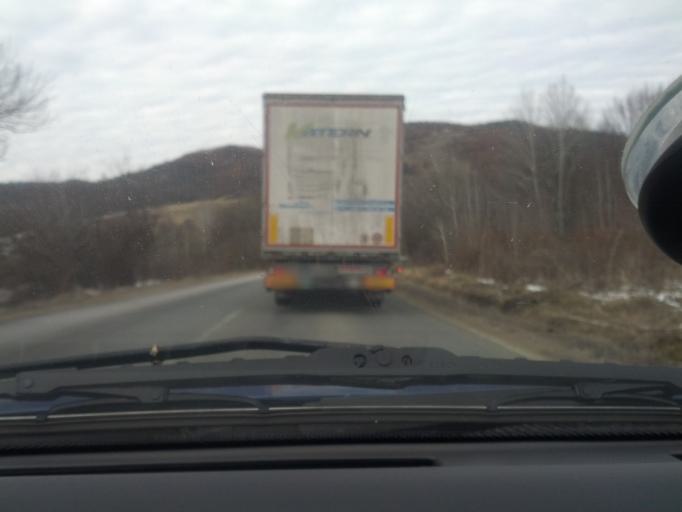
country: BG
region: Vratsa
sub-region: Obshtina Mezdra
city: Mezdra
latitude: 43.0252
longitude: 23.6672
